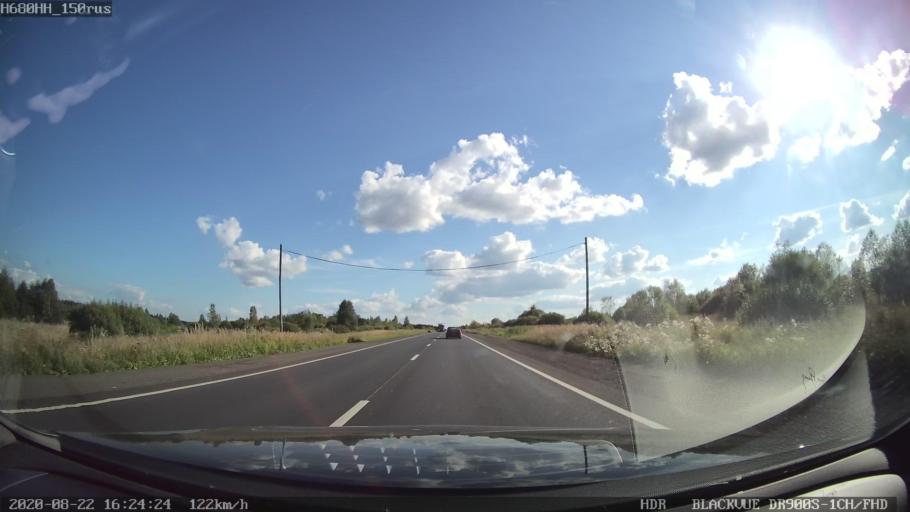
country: RU
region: Tverskaya
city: Rameshki
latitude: 57.3378
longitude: 36.0955
